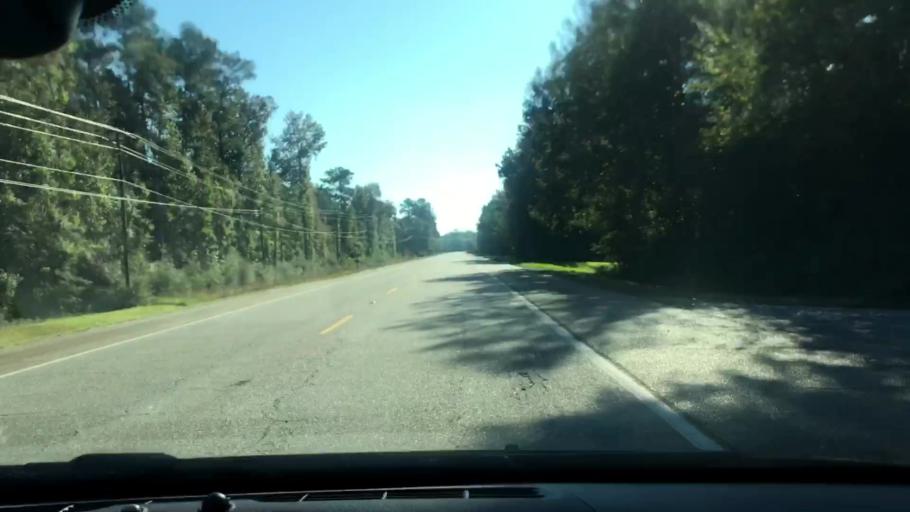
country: US
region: Mississippi
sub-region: Pearl River County
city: Nicholson
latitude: 30.5182
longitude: -89.8362
